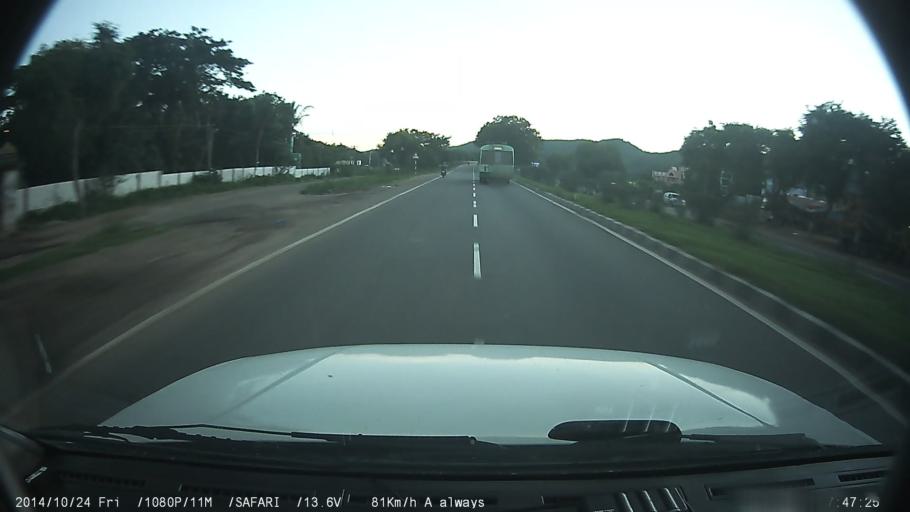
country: IN
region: Tamil Nadu
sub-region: Kancheepuram
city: Singapperumalkovil
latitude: 12.7377
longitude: 79.9881
